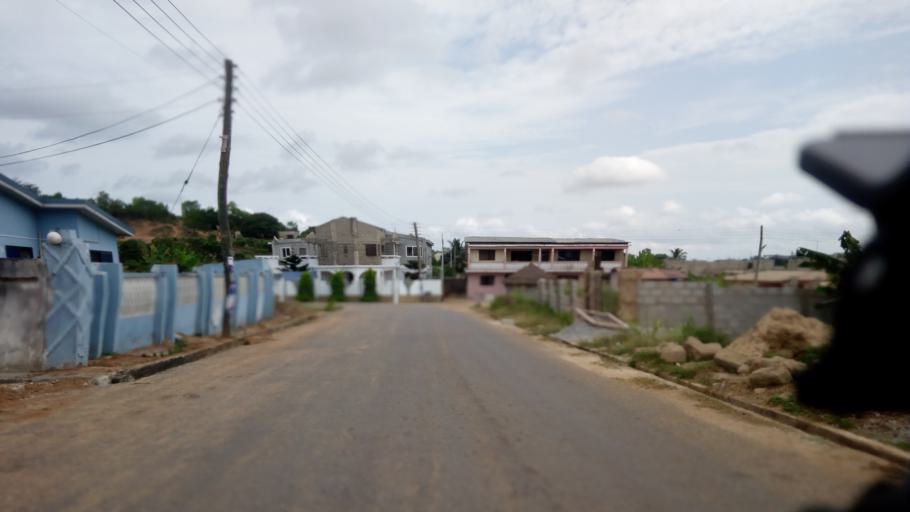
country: GH
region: Central
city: Cape Coast
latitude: 5.1072
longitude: -1.2714
